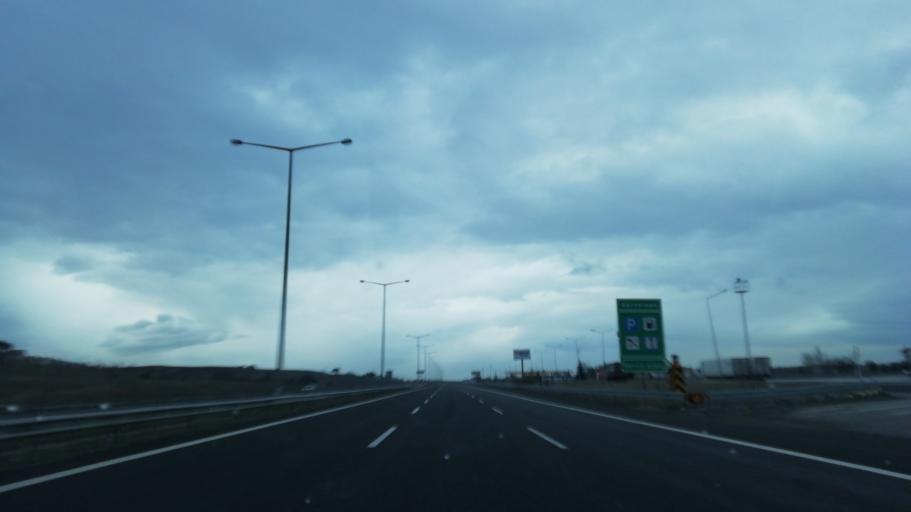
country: TR
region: Bolu
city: Dortdivan
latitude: 40.7512
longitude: 32.0802
